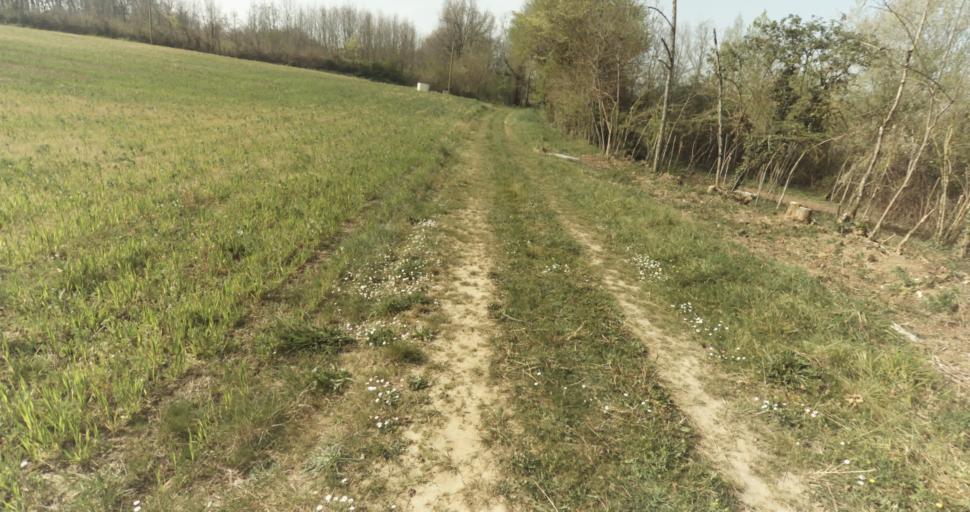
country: FR
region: Midi-Pyrenees
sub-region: Departement du Tarn-et-Garonne
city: Lafrancaise
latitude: 44.1349
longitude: 1.1717
